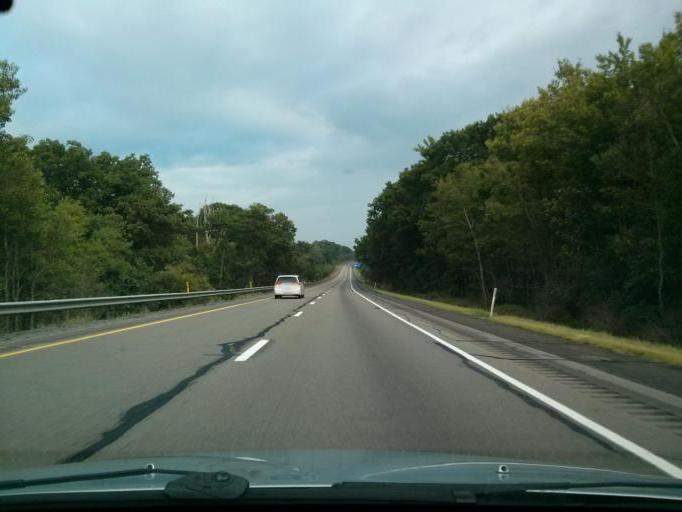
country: US
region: Pennsylvania
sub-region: Jefferson County
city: Brookville
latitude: 41.1785
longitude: -79.1294
